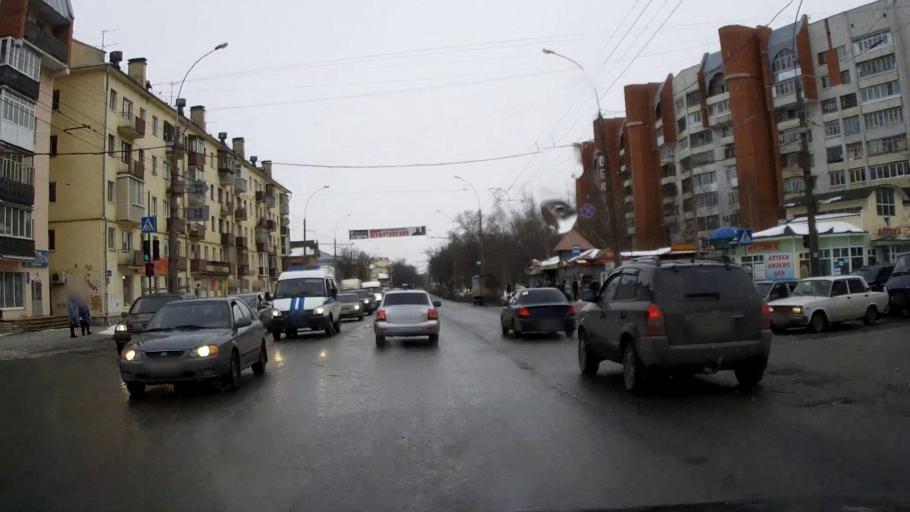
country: RU
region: Vologda
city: Vologda
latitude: 59.2194
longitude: 39.8676
